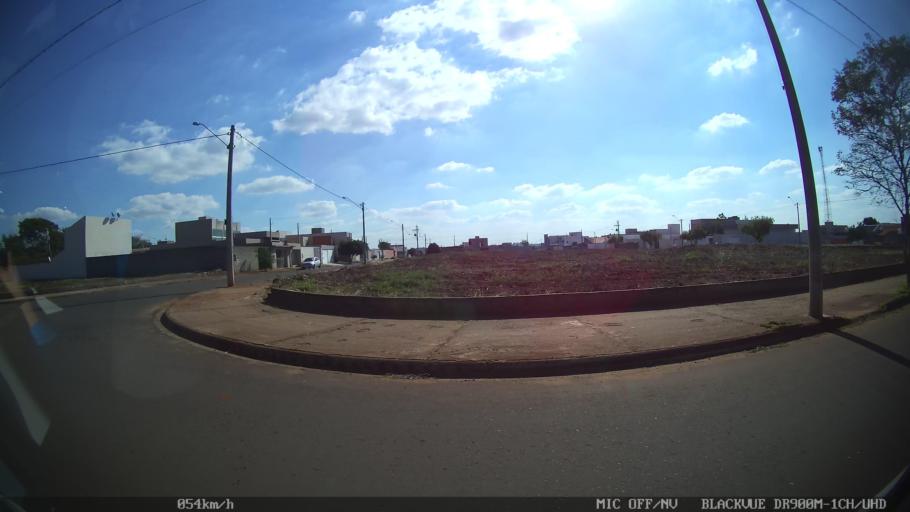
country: BR
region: Sao Paulo
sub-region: Sumare
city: Sumare
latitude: -22.8228
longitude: -47.2912
